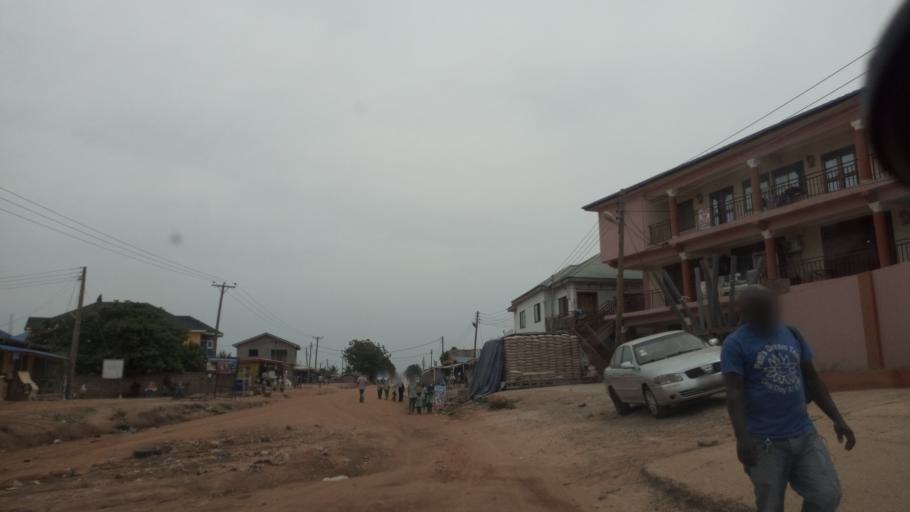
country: GH
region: Greater Accra
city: Medina Estates
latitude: 5.7071
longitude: -0.1322
